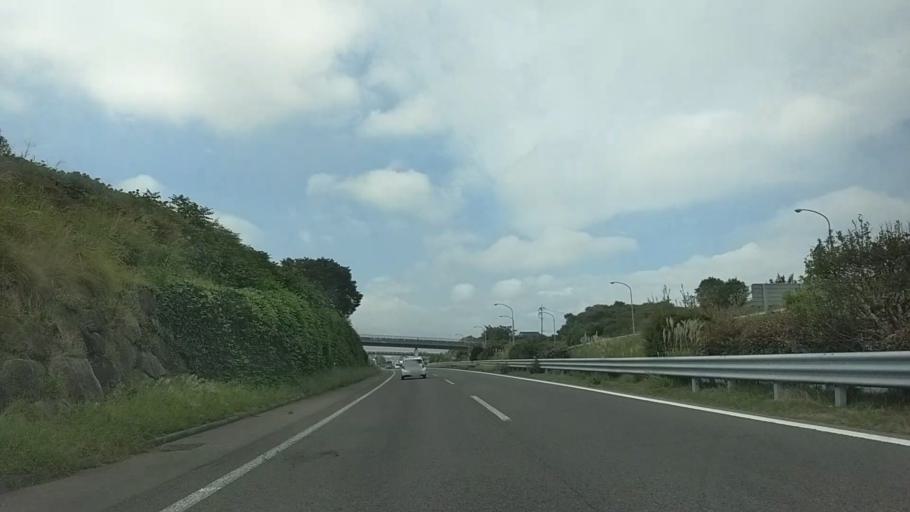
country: JP
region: Yamanashi
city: Enzan
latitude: 35.6454
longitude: 138.7147
